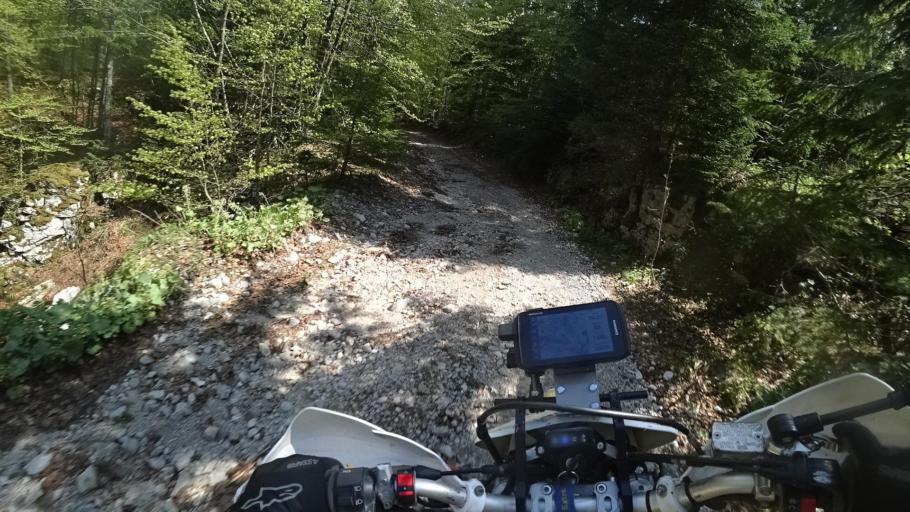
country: BA
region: Republika Srpska
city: Sipovo
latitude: 44.1369
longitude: 17.0252
